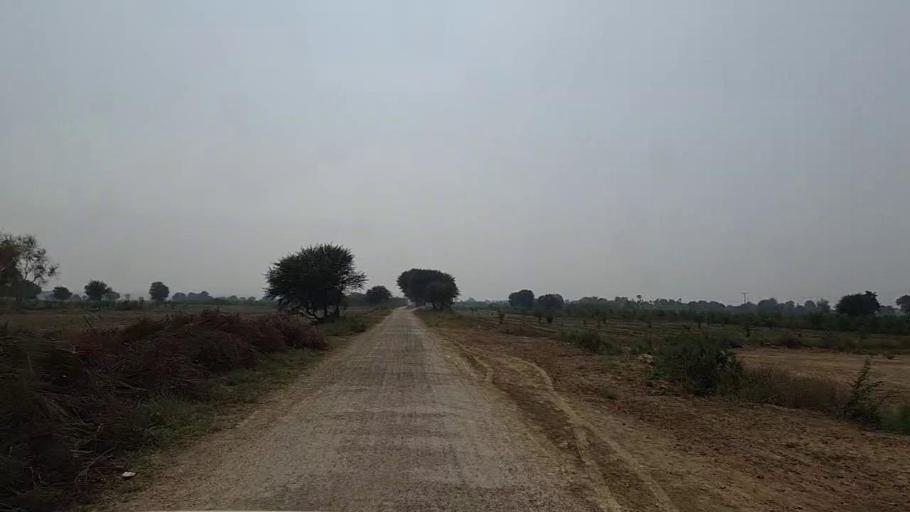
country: PK
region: Sindh
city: Naukot
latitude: 24.8238
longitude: 69.3994
